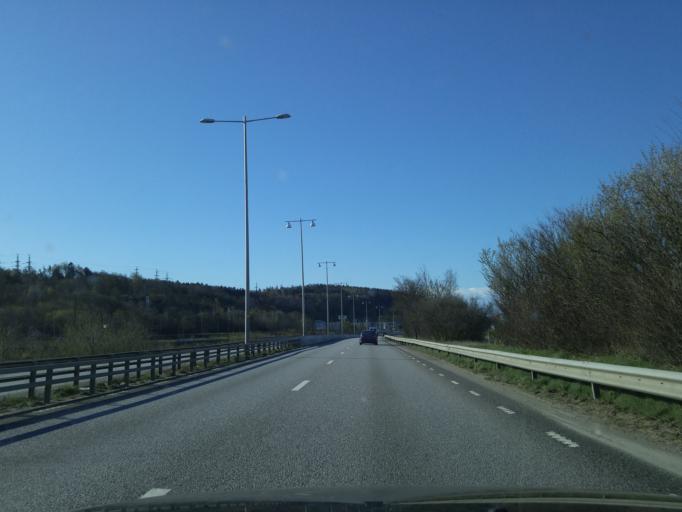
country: SE
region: Vaestra Goetaland
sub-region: Goteborg
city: Eriksbo
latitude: 57.7497
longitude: 12.0063
